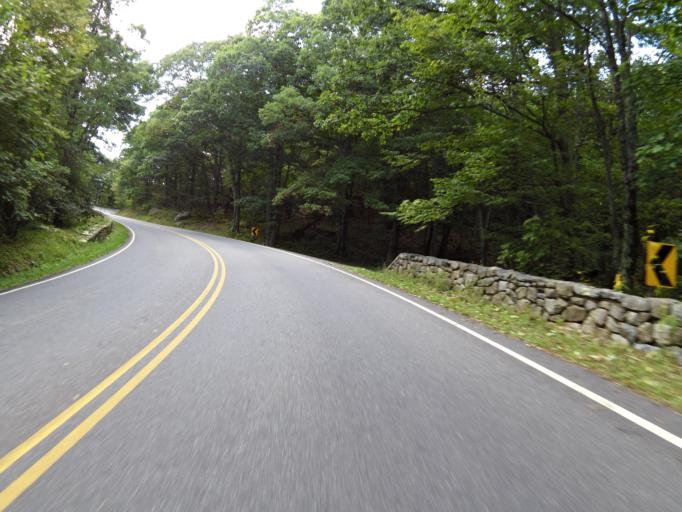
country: US
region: Virginia
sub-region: Page County
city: Stanley
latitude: 38.5569
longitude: -78.3786
